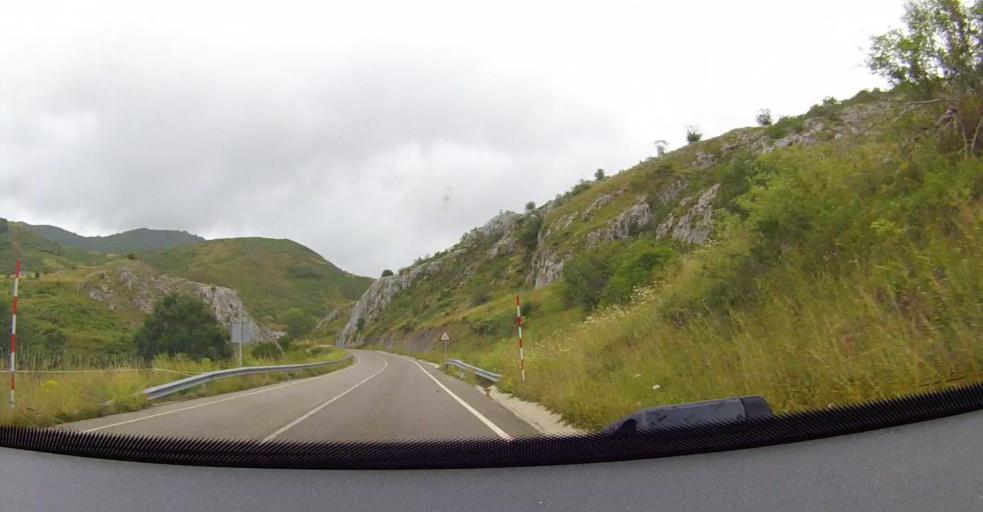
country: ES
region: Castille and Leon
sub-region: Provincia de Leon
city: Acebedo
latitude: 43.0674
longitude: -5.1405
